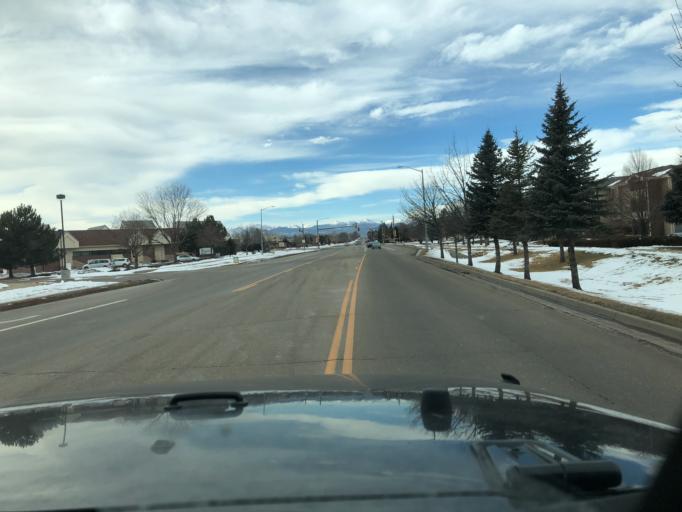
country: US
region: Colorado
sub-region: Boulder County
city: Longmont
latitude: 40.1888
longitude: -105.0716
